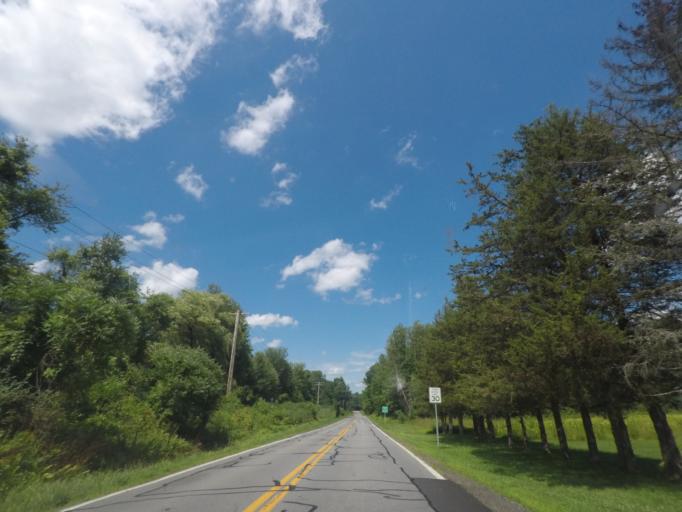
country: US
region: New York
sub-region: Schenectady County
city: Rotterdam
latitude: 42.7294
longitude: -73.9535
